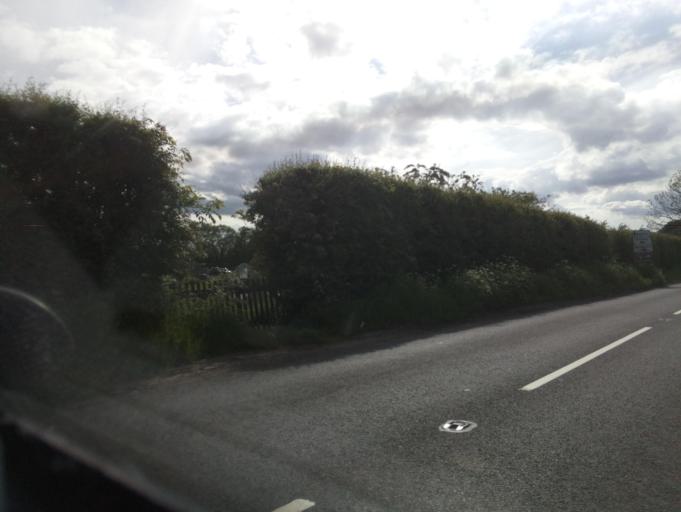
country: GB
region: England
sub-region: Worcestershire
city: Broadway
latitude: 52.0704
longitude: -1.8218
